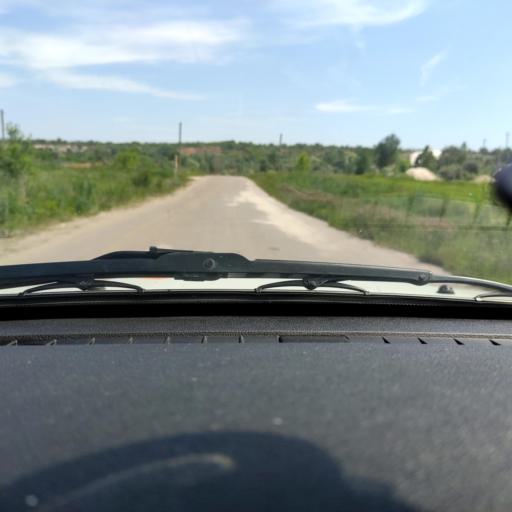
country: RU
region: Voronezj
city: Devitsa
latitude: 51.6249
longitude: 38.9527
